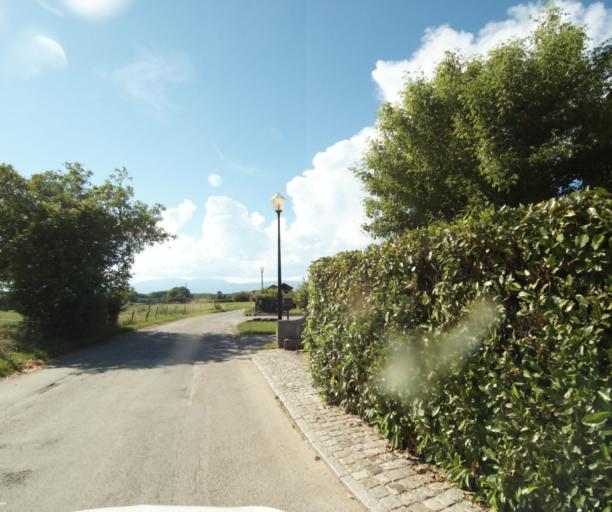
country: FR
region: Rhone-Alpes
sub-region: Departement de la Haute-Savoie
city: Massongy
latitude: 46.3230
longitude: 6.3207
